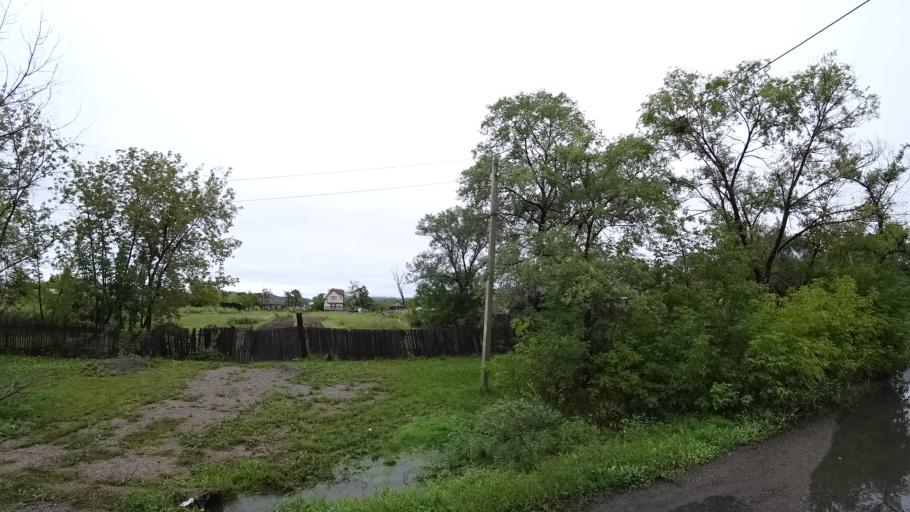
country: RU
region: Primorskiy
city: Monastyrishche
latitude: 44.1992
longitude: 132.4666
